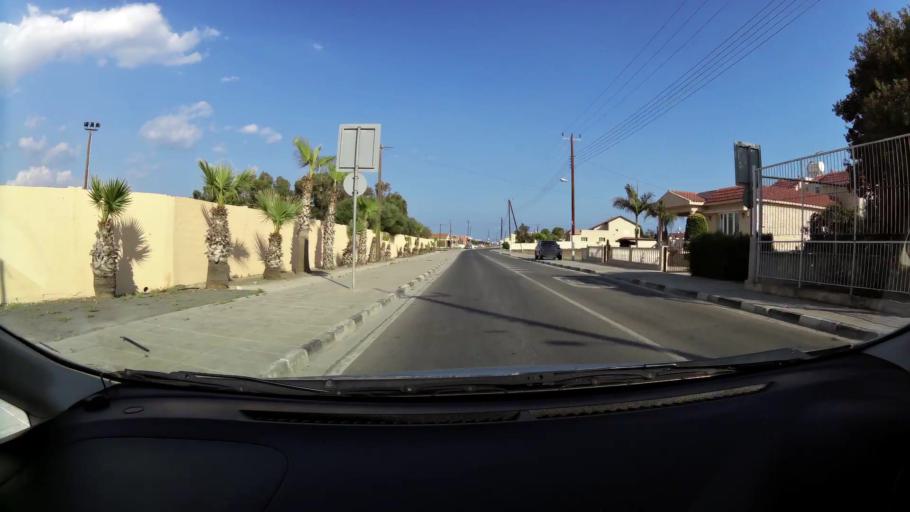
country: CY
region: Larnaka
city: Dhromolaxia
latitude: 34.8766
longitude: 33.5903
